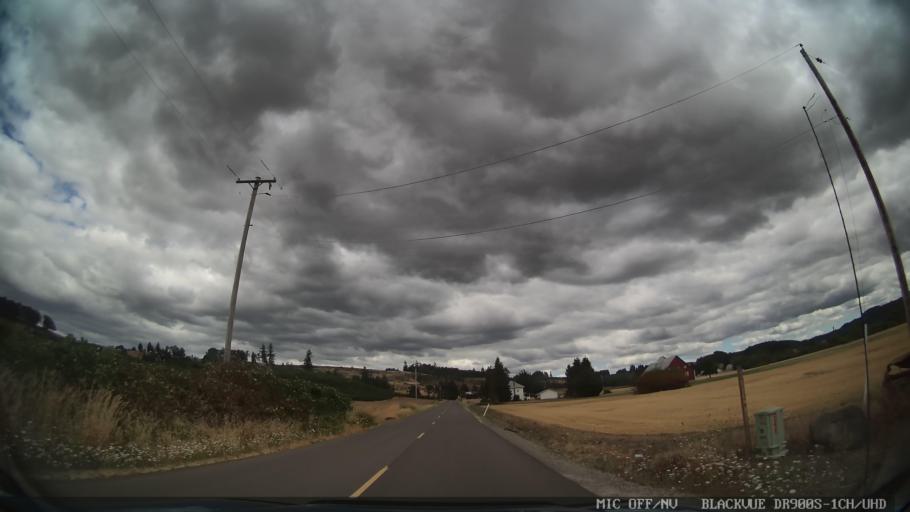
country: US
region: Oregon
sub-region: Marion County
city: Sublimity
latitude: 44.8726
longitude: -122.7145
